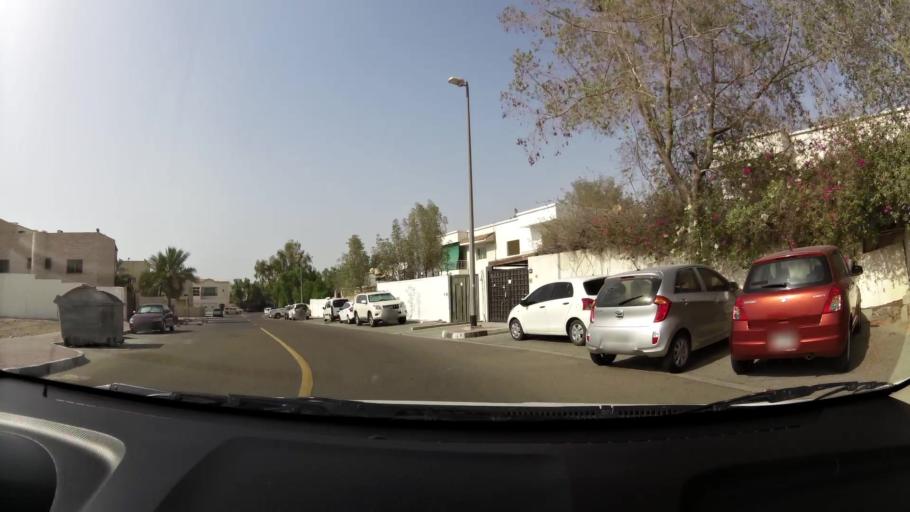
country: AE
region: Ash Shariqah
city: Sharjah
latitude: 25.2426
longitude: 55.3498
